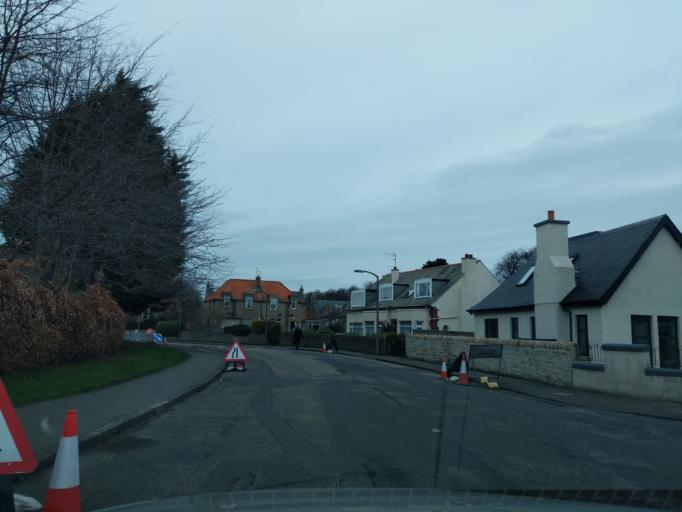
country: GB
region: Scotland
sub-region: Edinburgh
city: Colinton
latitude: 55.9369
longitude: -3.2850
